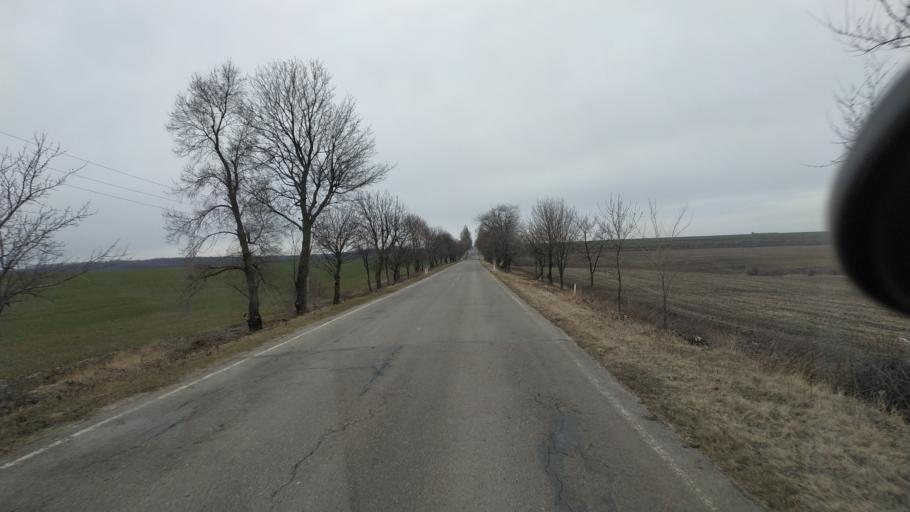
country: MD
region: Telenesti
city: Cocieri
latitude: 47.3651
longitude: 29.0428
